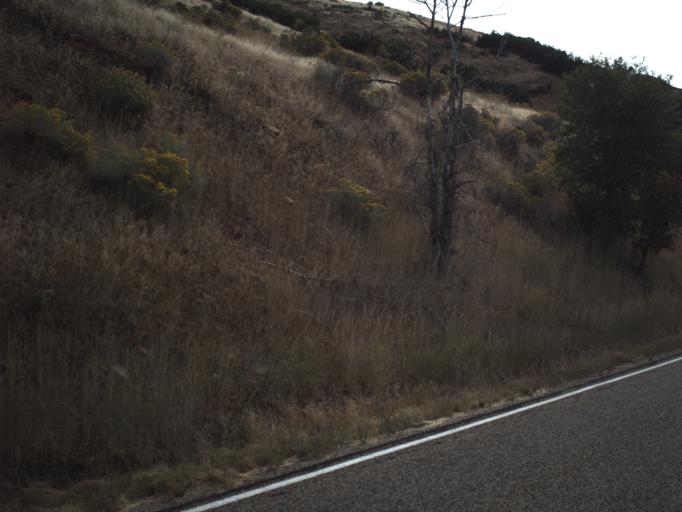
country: US
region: Utah
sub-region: Morgan County
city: Morgan
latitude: 40.9370
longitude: -111.6371
